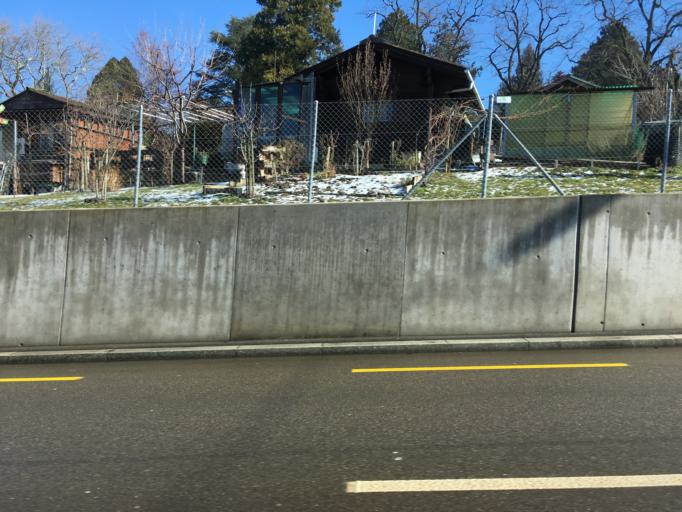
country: CH
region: Zurich
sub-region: Bezirk Zuerich
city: Zuerich (Kreis 8) / Weinegg
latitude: 47.3520
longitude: 8.5780
